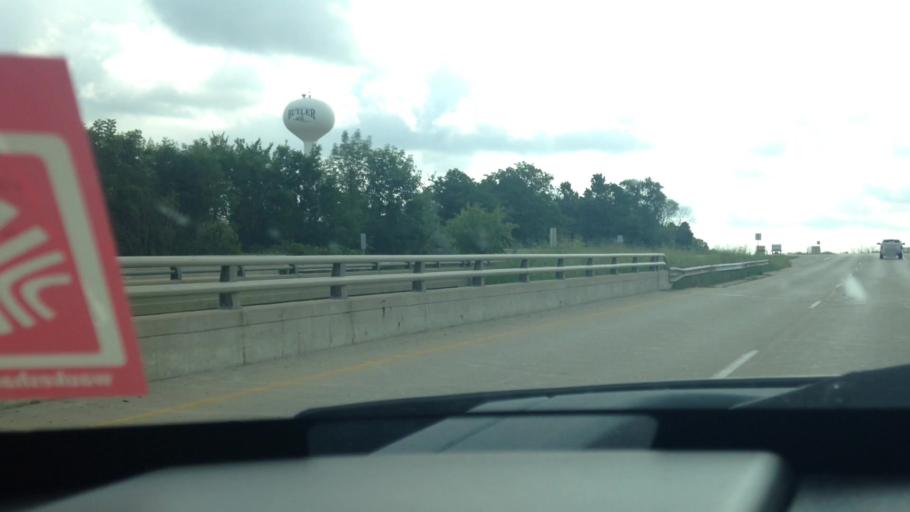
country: US
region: Wisconsin
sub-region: Waukesha County
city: Butler
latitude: 43.1181
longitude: -88.0755
